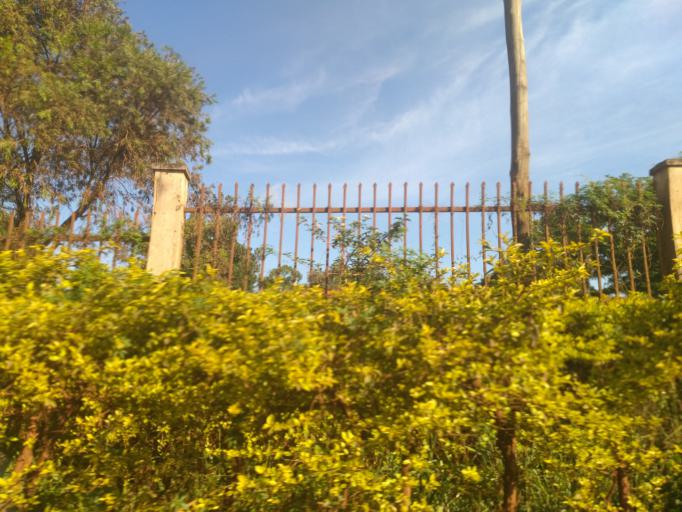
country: UG
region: Eastern Region
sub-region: Jinja District
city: Jinja
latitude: 0.4457
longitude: 33.1959
